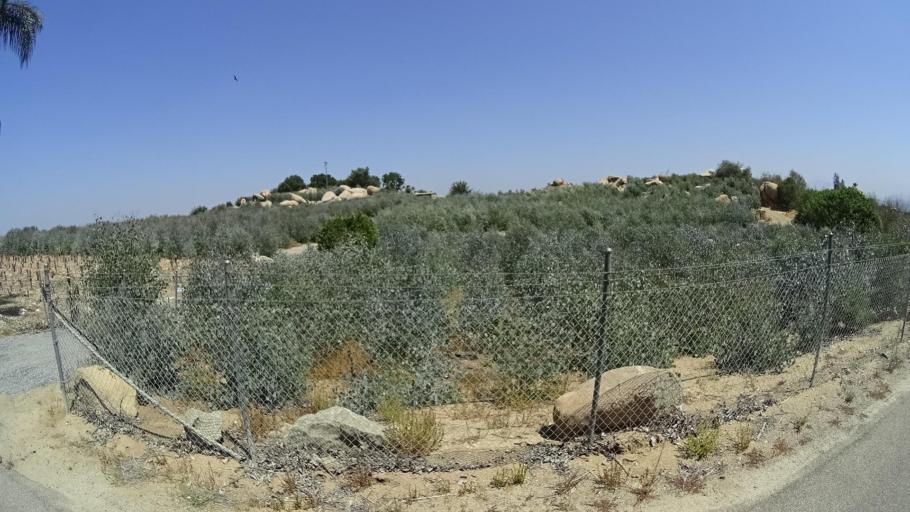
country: US
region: California
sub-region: San Diego County
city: Fallbrook
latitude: 33.4277
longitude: -117.2695
